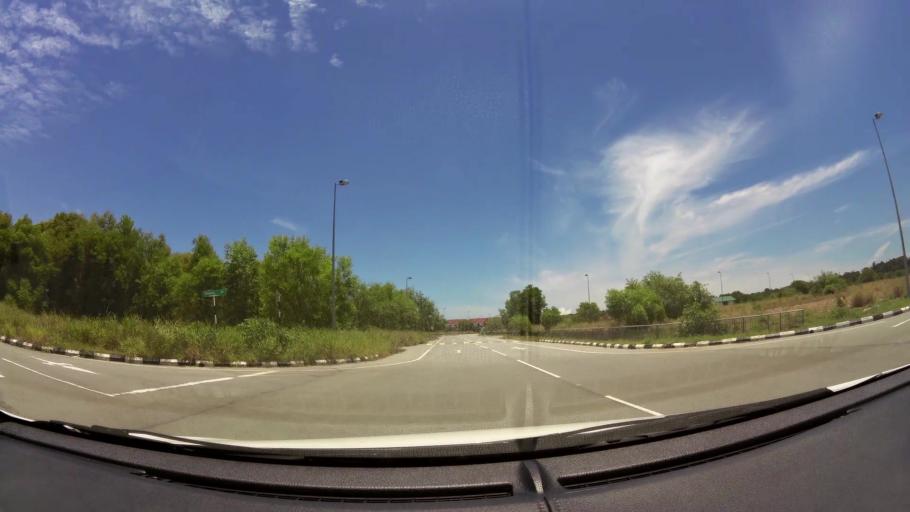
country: BN
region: Brunei and Muara
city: Bandar Seri Begawan
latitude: 5.0091
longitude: 115.0062
